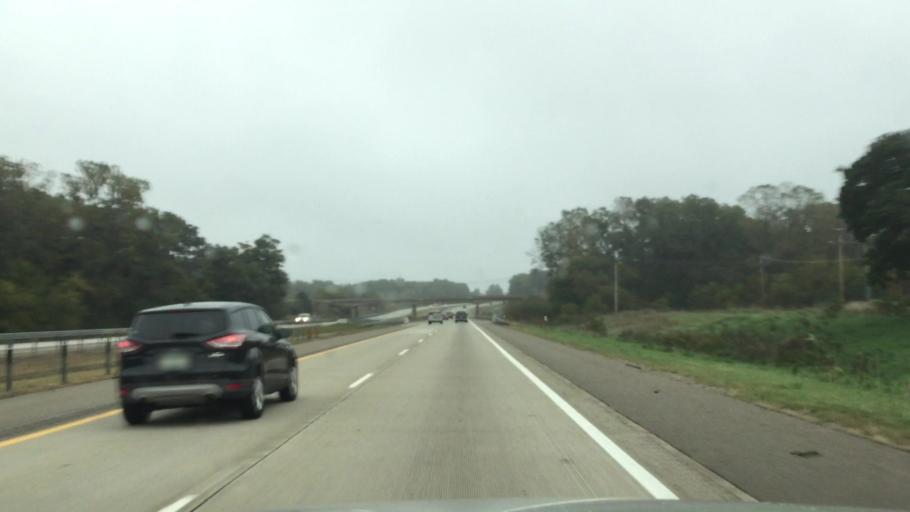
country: US
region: Michigan
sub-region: Van Buren County
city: Paw Paw
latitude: 42.2133
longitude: -85.8654
